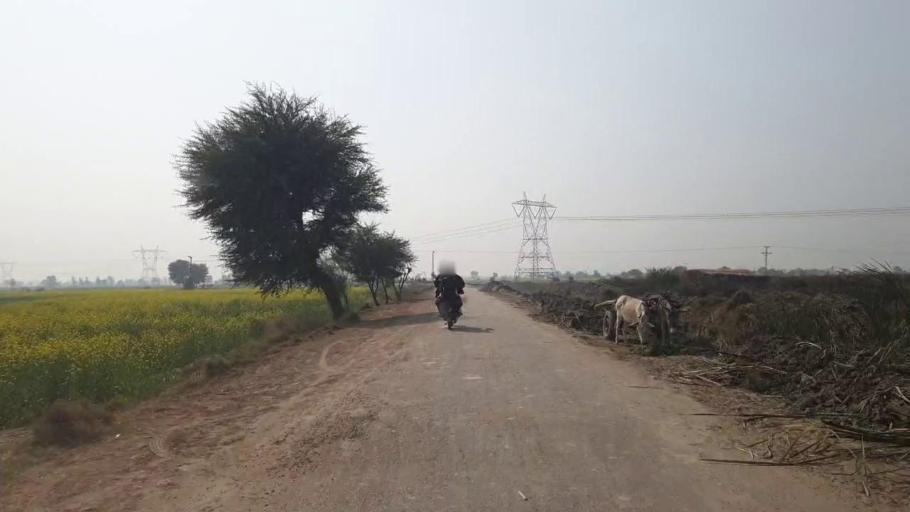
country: PK
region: Sindh
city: Hala
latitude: 25.9422
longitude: 68.4489
